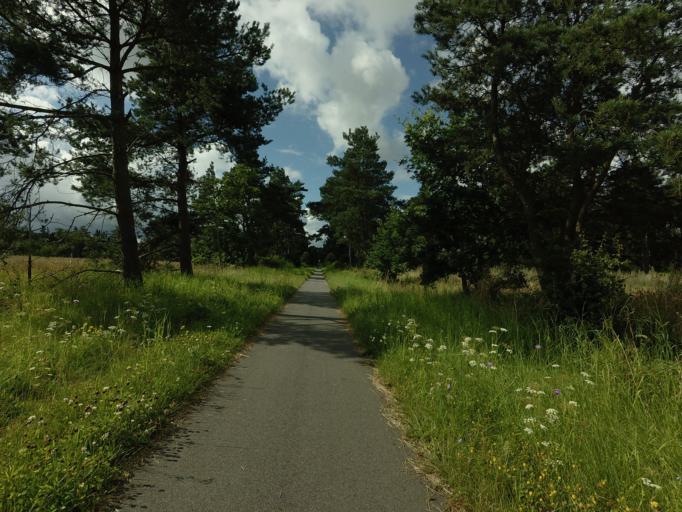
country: DK
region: Central Jutland
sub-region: Silkeborg Kommune
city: Svejbaek
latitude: 56.2038
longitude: 9.6694
